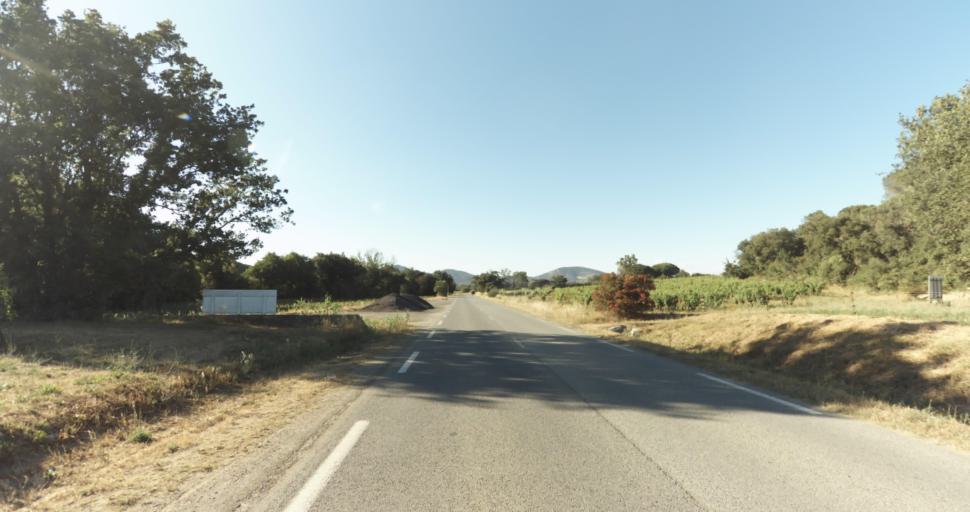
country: FR
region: Provence-Alpes-Cote d'Azur
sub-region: Departement du Var
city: Gassin
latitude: 43.2456
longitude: 6.5946
